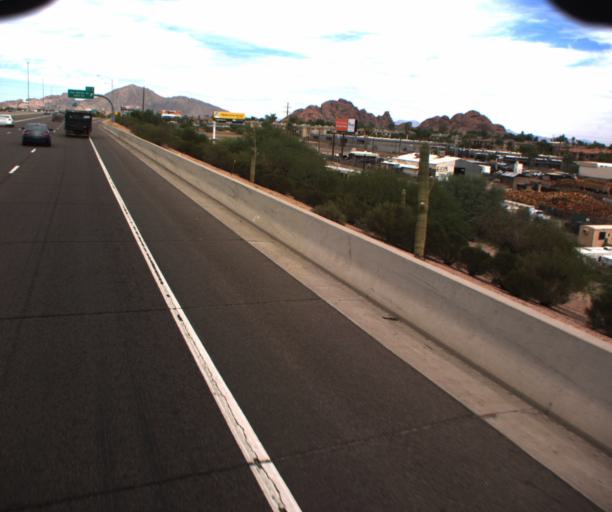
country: US
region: Arizona
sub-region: Maricopa County
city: Tempe Junction
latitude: 33.4440
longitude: -111.9687
